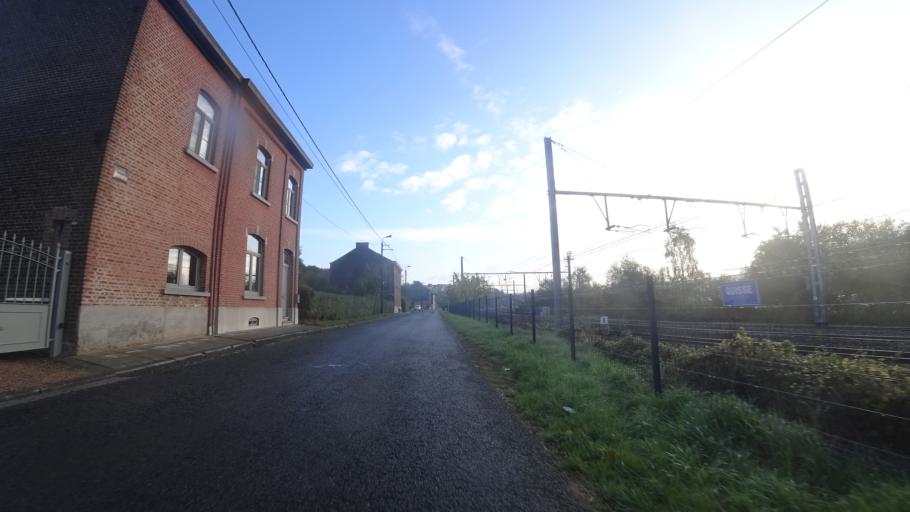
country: BE
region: Wallonia
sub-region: Province de Namur
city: Floreffe
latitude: 50.4558
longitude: 4.8006
